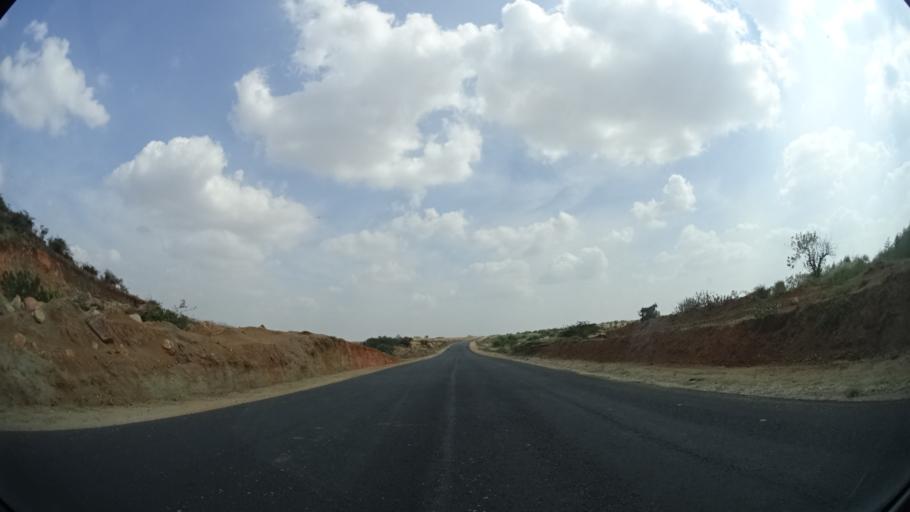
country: IN
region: Andhra Pradesh
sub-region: Anantapur
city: Uravakonda
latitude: 14.7907
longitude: 77.3640
